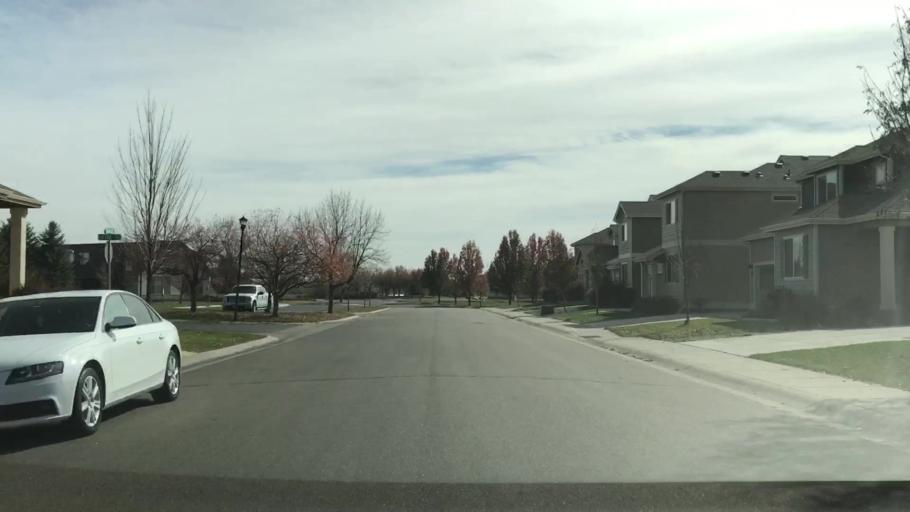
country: US
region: Colorado
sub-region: Larimer County
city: Fort Collins
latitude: 40.5910
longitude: -105.0418
